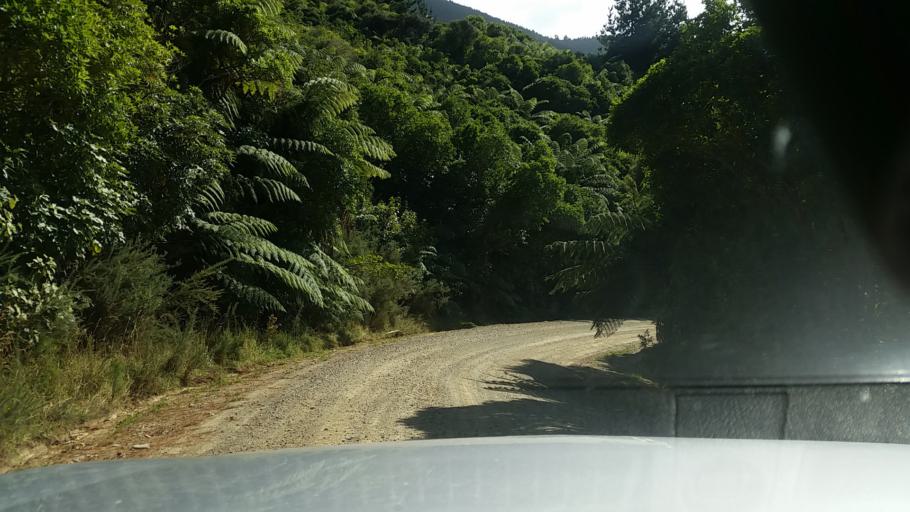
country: NZ
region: Marlborough
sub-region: Marlborough District
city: Picton
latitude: -41.2877
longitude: 174.1756
